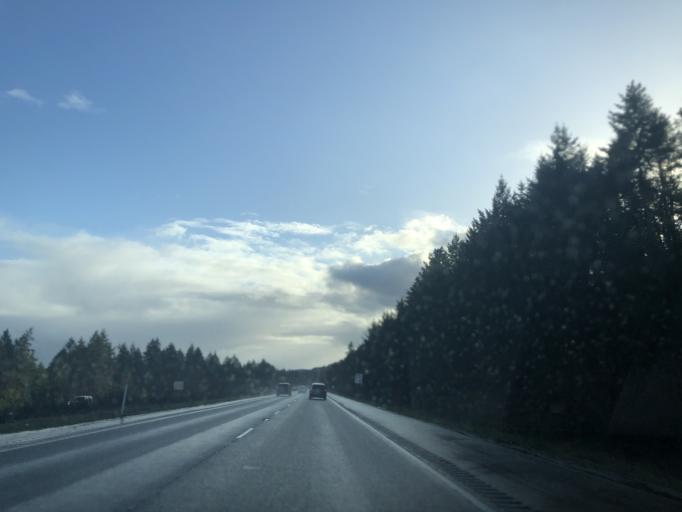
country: US
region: Washington
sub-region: Kitsap County
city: Chico
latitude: 47.6277
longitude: -122.7108
